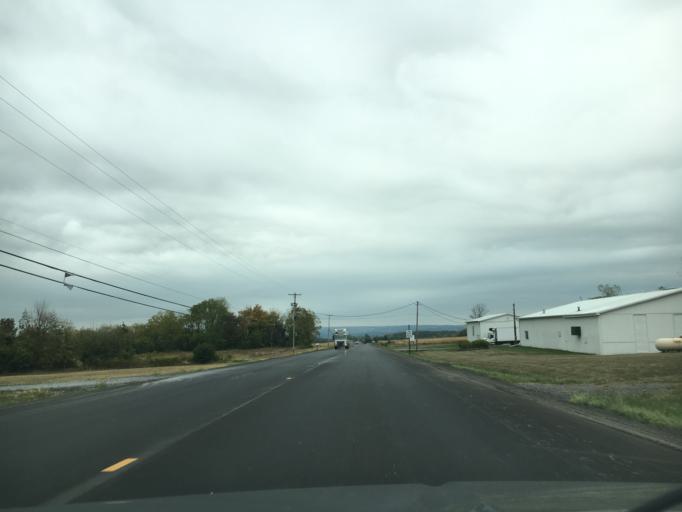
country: US
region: New York
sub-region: Cayuga County
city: Union Springs
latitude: 42.6814
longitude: -76.8002
